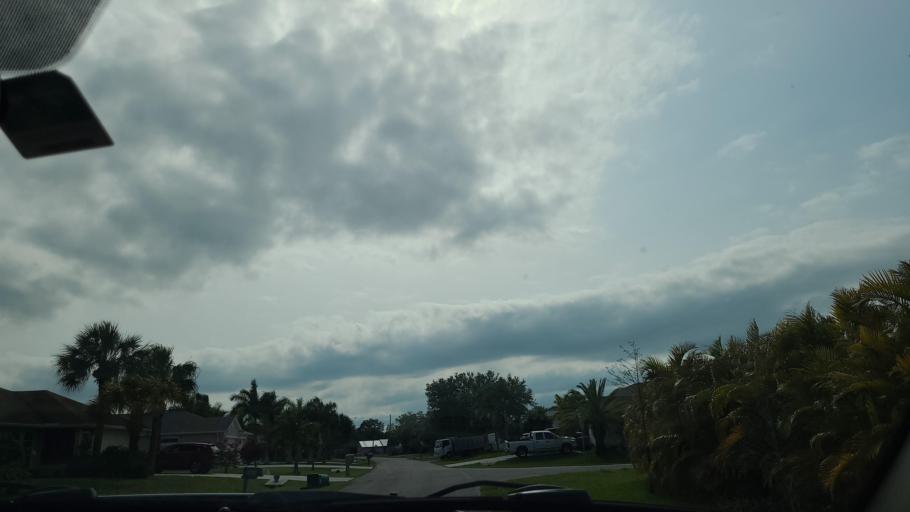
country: US
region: Florida
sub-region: Indian River County
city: Sebastian
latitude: 27.7685
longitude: -80.4741
